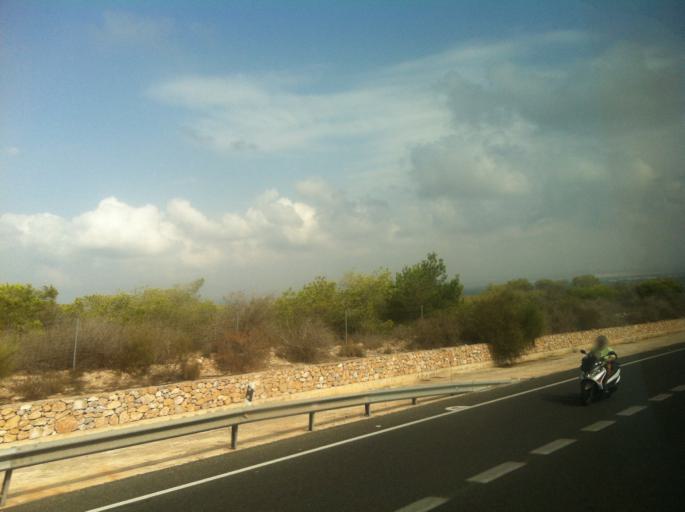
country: ES
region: Valencia
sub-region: Provincia de Alicante
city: Guardamar del Segura
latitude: 38.1501
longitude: -0.6572
